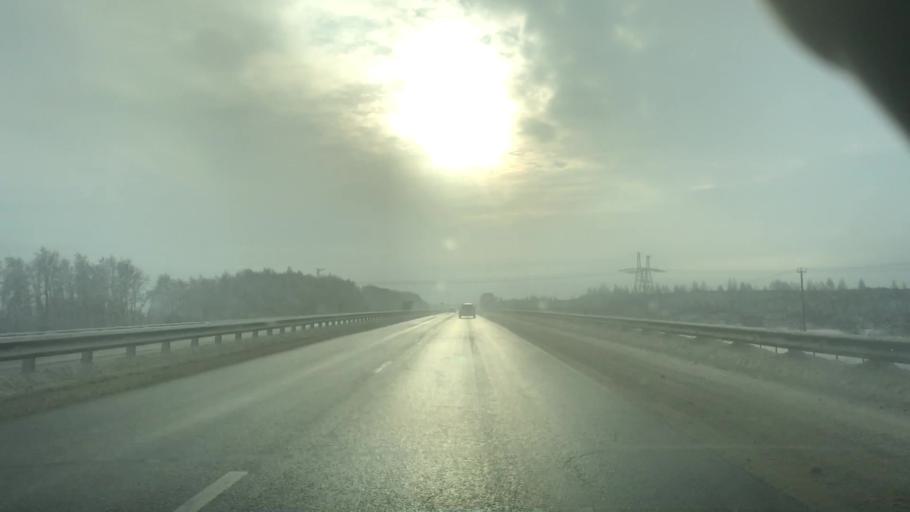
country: RU
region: Tula
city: Venev
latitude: 54.2943
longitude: 38.1576
